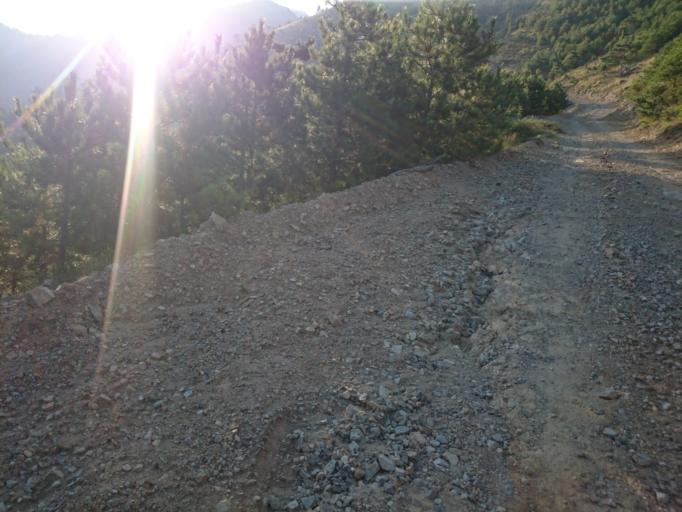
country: AL
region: Lezhe
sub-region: Rrethi i Mirdites
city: Orosh
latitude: 41.8668
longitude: 20.0839
